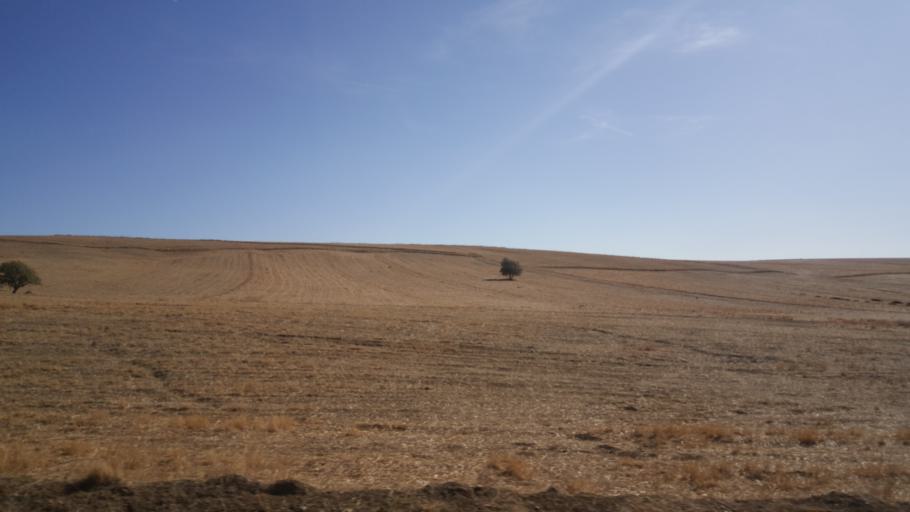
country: TR
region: Ankara
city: Yenice
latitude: 39.2903
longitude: 32.6267
